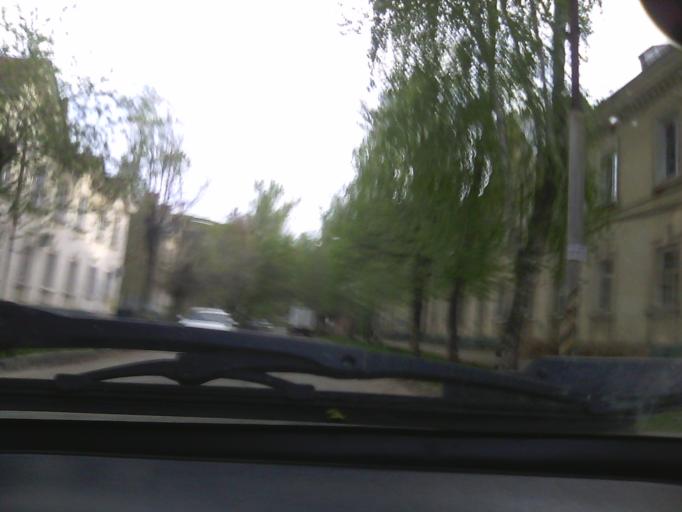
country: RU
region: Saratov
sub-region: Saratovskiy Rayon
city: Saratov
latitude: 51.5879
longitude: 45.9389
